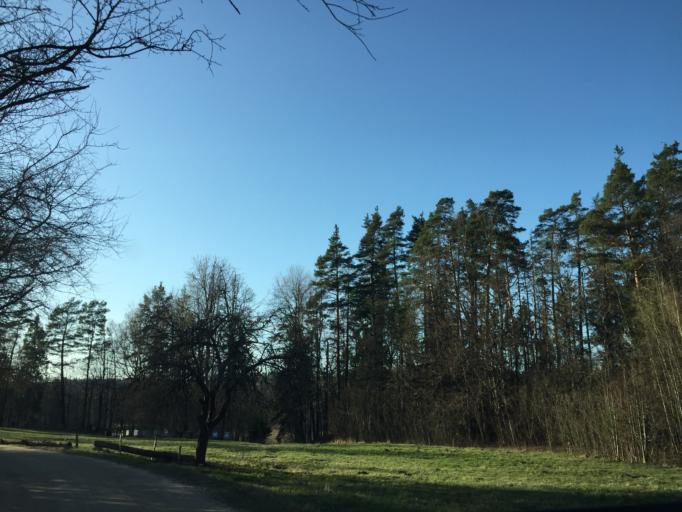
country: LV
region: Sigulda
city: Sigulda
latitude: 57.1438
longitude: 24.8081
